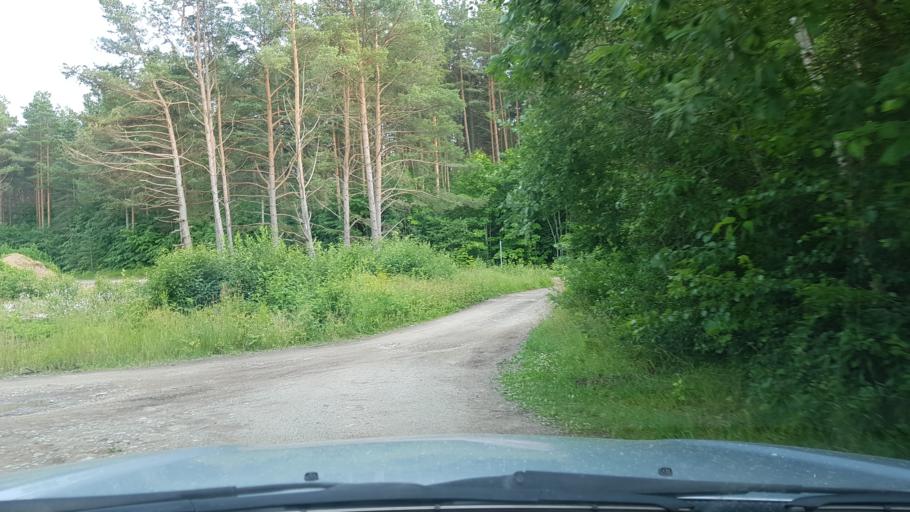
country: EE
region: Ida-Virumaa
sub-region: Narva-Joesuu linn
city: Narva-Joesuu
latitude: 59.4587
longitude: 28.0644
